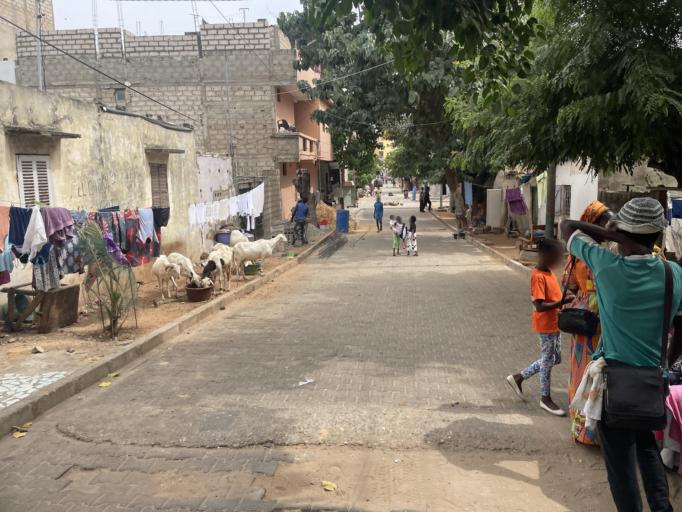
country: SN
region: Dakar
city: Grand Dakar
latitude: 14.7209
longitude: -17.4373
